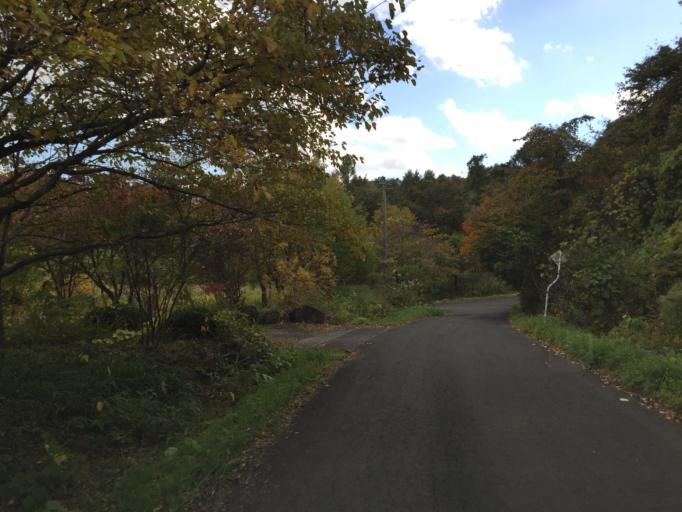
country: JP
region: Fukushima
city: Fukushima-shi
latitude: 37.7075
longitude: 140.3333
